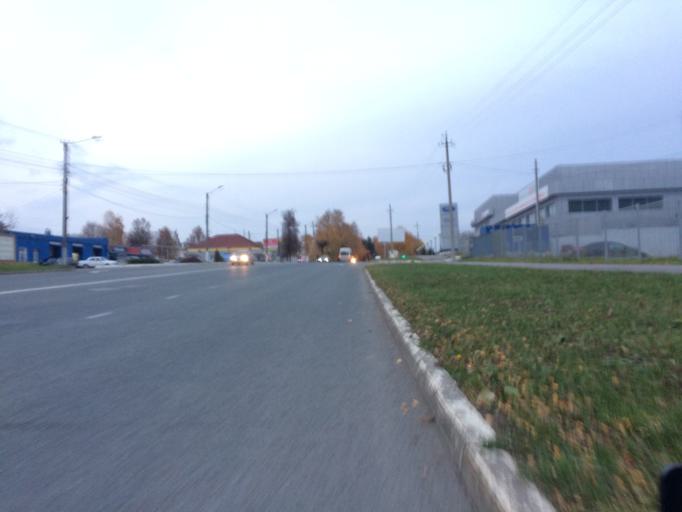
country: RU
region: Mariy-El
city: Yoshkar-Ola
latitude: 56.6059
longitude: 47.8808
